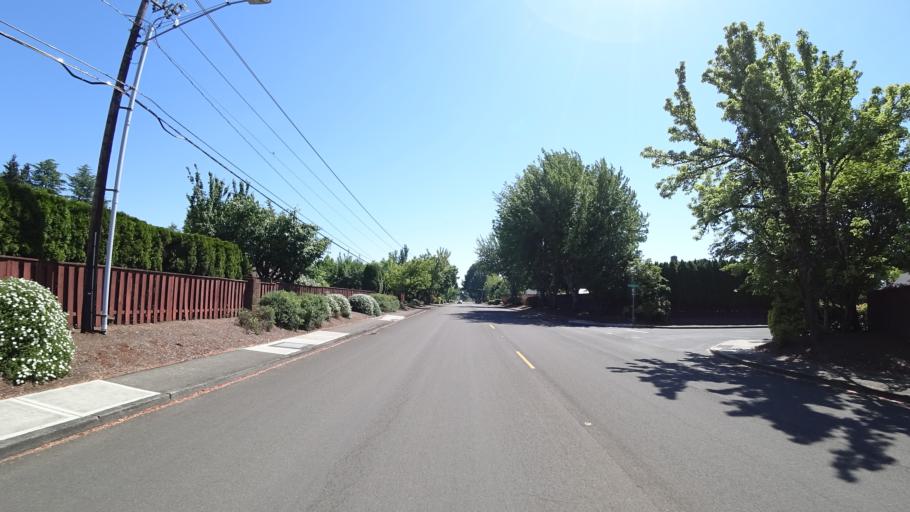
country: US
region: Oregon
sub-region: Washington County
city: Rockcreek
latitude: 45.5365
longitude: -122.9260
